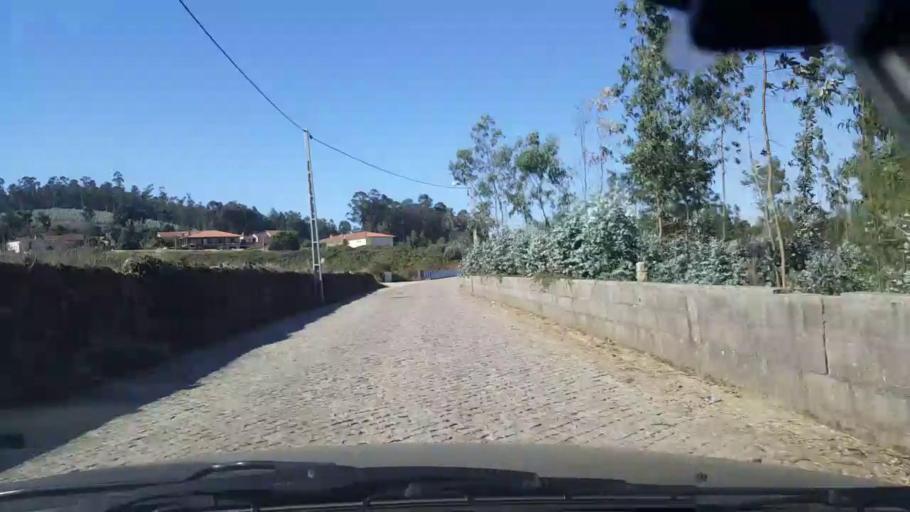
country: PT
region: Braga
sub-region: Vila Nova de Famalicao
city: Ribeirao
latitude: 41.3808
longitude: -8.6397
